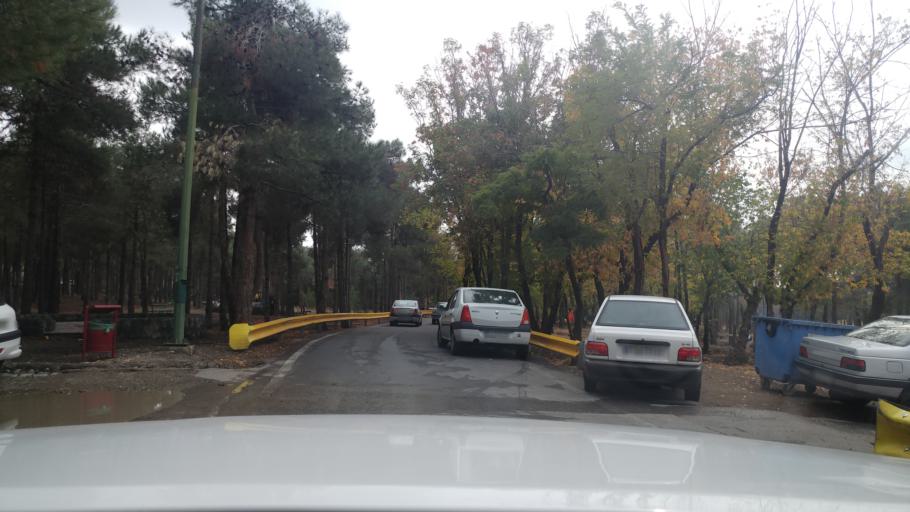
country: IR
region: Tehran
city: Shahr-e Qods
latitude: 35.7247
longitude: 51.2223
